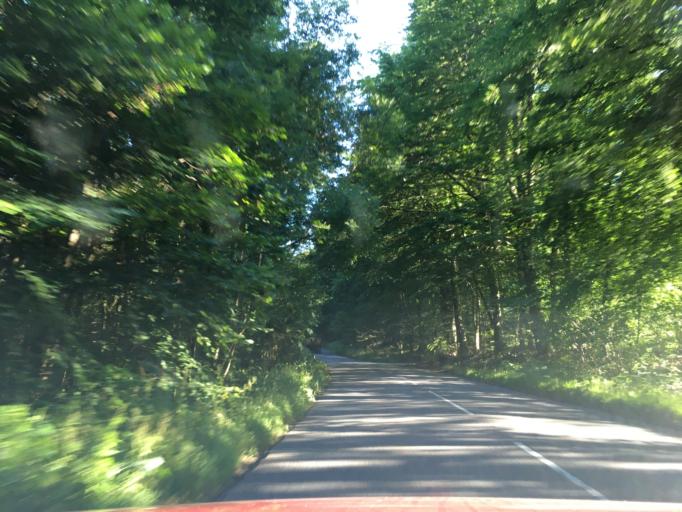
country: GB
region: Wales
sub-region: Monmouthshire
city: Tintern
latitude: 51.6690
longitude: -2.7489
